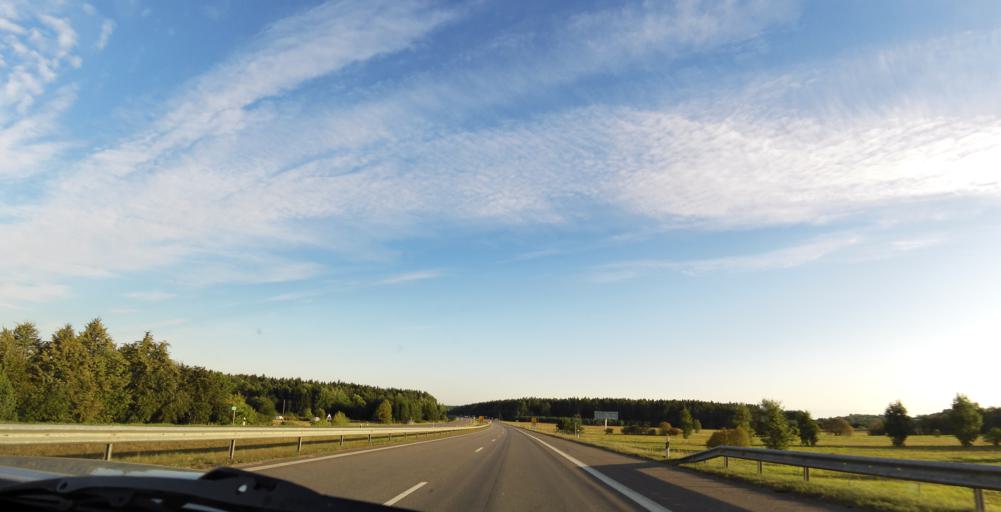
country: LT
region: Vilnius County
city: Ukmerge
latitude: 55.2370
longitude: 24.8212
